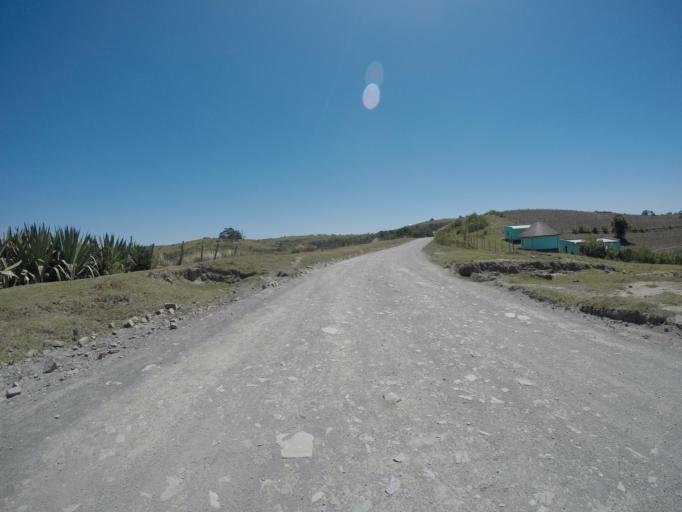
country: ZA
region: Eastern Cape
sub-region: OR Tambo District Municipality
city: Libode
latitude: -31.9923
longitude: 29.0538
